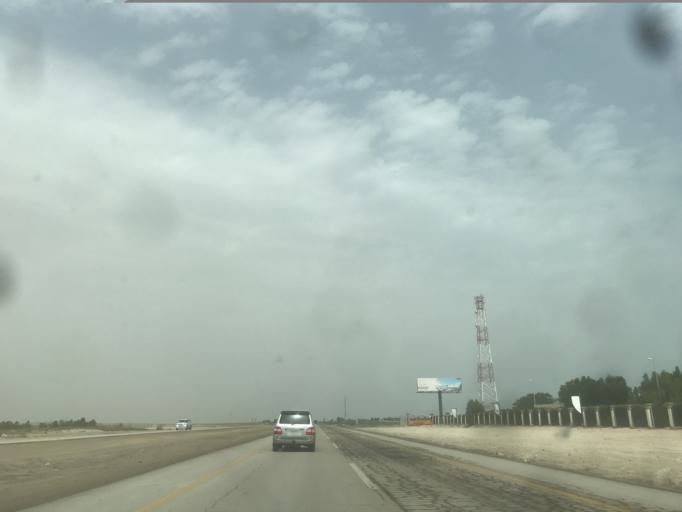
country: SA
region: Eastern Province
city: Dhahran
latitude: 26.0310
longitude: 49.9927
